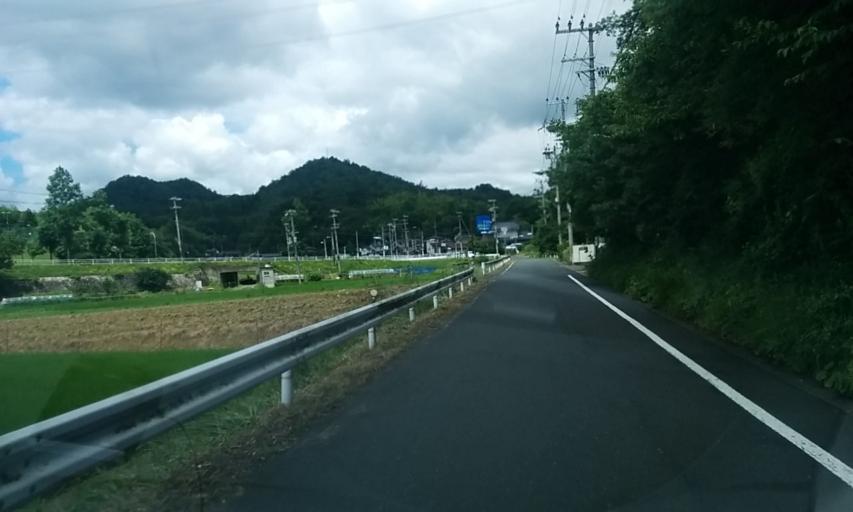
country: JP
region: Kyoto
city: Ayabe
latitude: 35.3249
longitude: 135.2774
